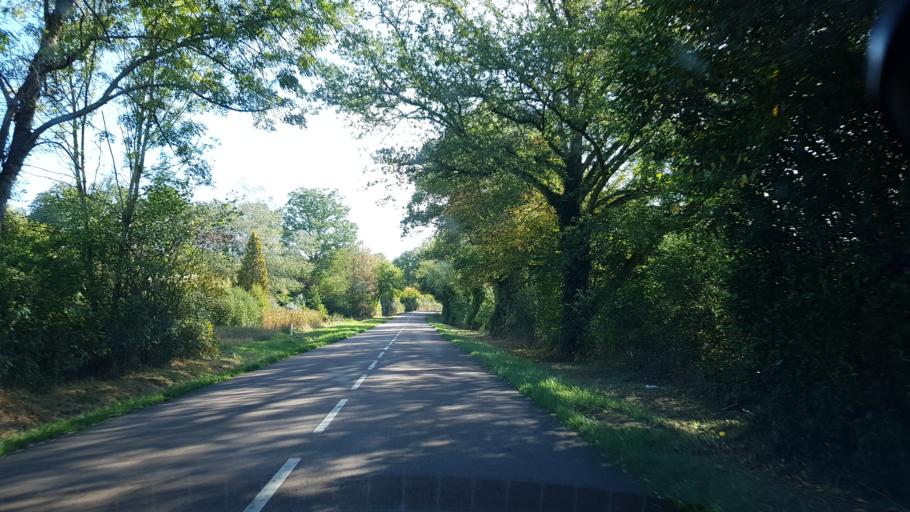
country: FR
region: Bourgogne
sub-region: Departement de la Nievre
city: Saint-Amand-en-Puisaye
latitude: 47.5333
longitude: 3.0466
